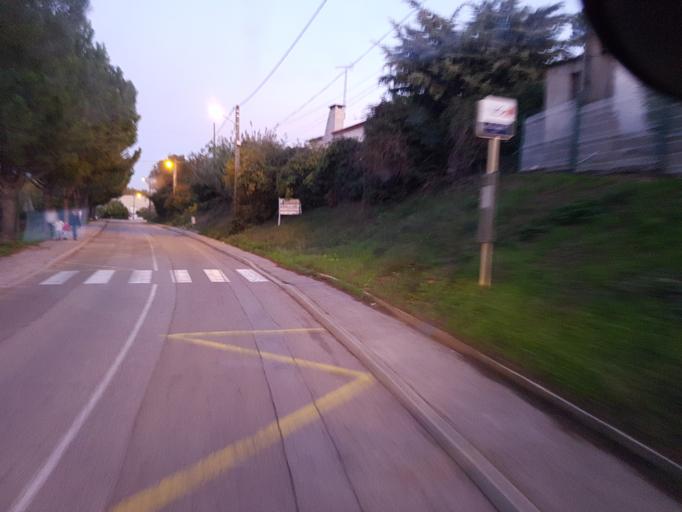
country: FR
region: Languedoc-Roussillon
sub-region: Departement du Gard
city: Bellegarde
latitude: 43.7570
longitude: 4.5082
